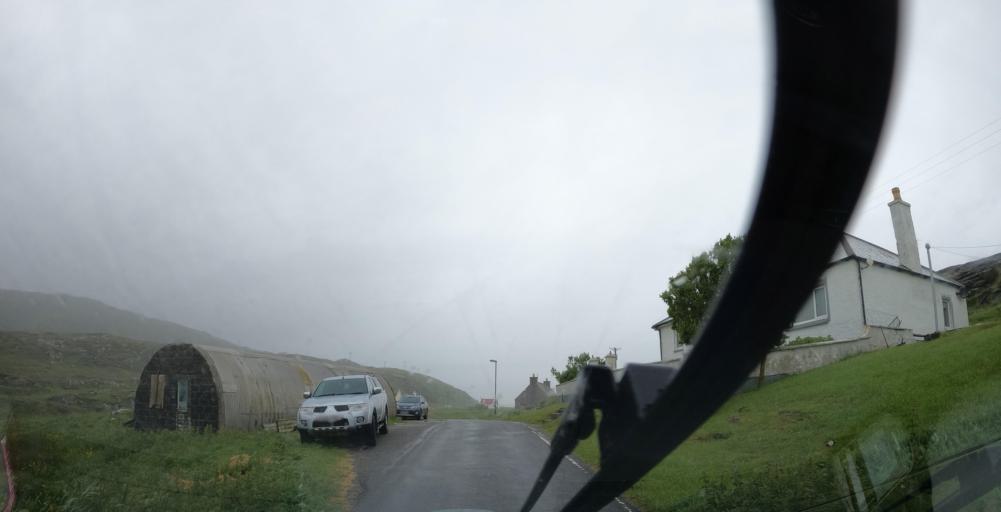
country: GB
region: Scotland
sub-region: Eilean Siar
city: Barra
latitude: 57.0126
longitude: -7.4283
